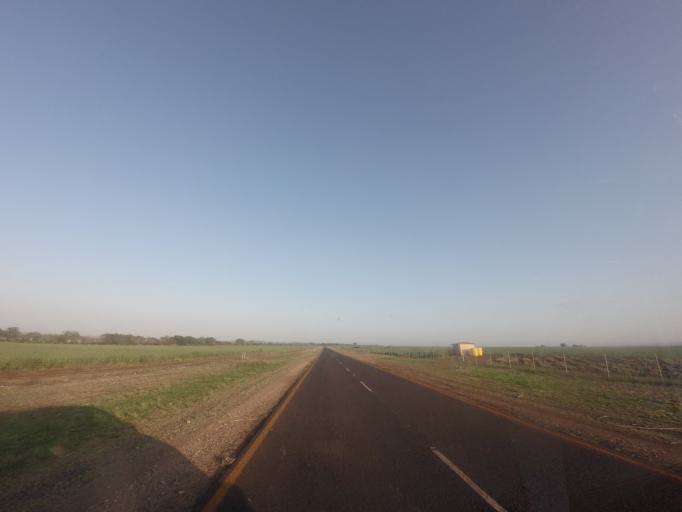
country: ZA
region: Mpumalanga
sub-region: Ehlanzeni District
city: Komatipoort
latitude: -25.4245
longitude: 31.9448
